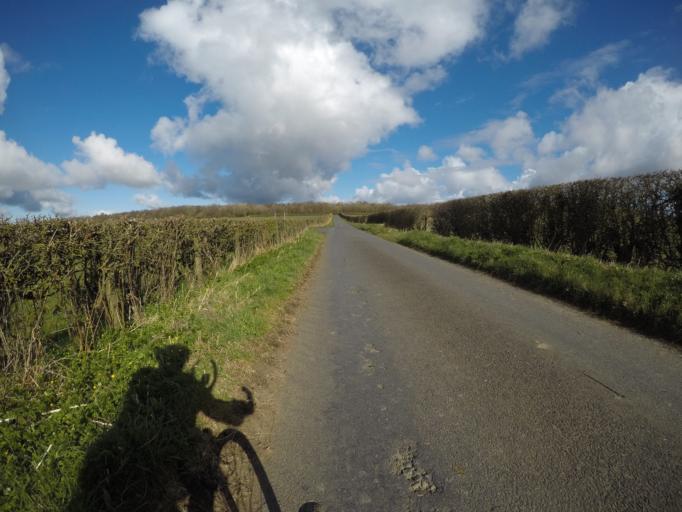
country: GB
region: Scotland
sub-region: North Ayrshire
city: Irvine
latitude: 55.6691
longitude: -4.6516
